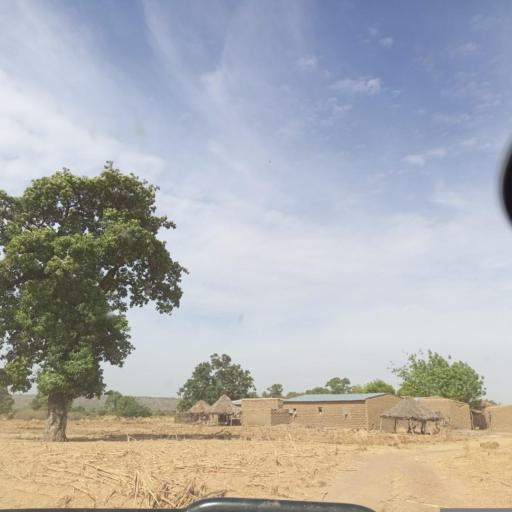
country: ML
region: Koulikoro
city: Koulikoro
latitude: 13.1269
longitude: -7.7082
